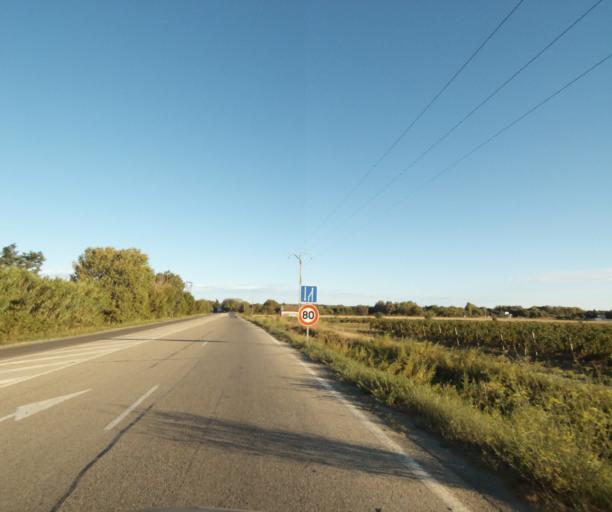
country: FR
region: Languedoc-Roussillon
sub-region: Departement du Gard
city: Caissargues
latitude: 43.8109
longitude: 4.4011
